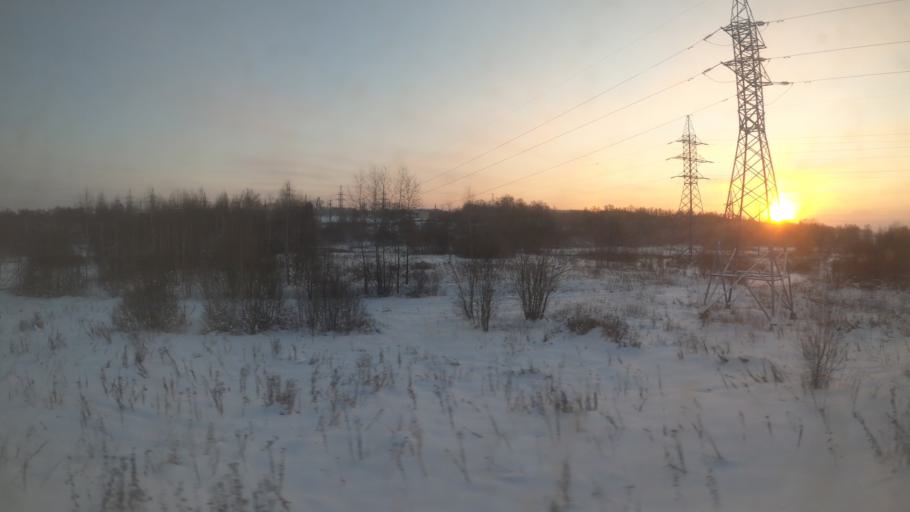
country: RU
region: Moskovskaya
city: Iksha
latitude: 56.1593
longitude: 37.5003
